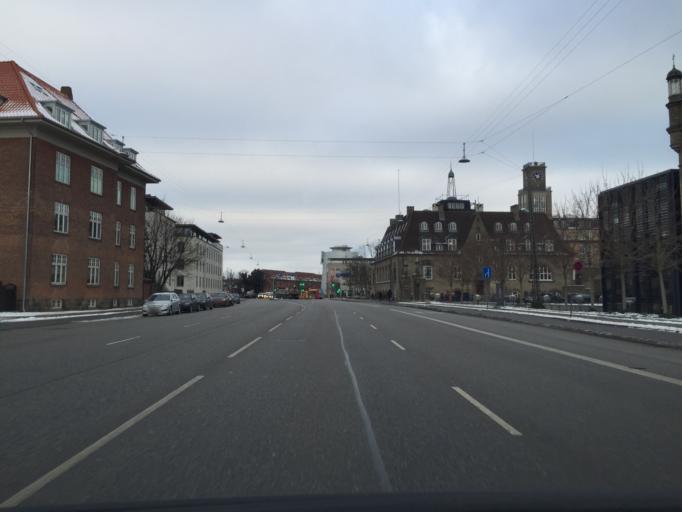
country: DK
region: Capital Region
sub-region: Gentofte Kommune
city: Charlottenlund
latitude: 55.7250
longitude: 12.5770
